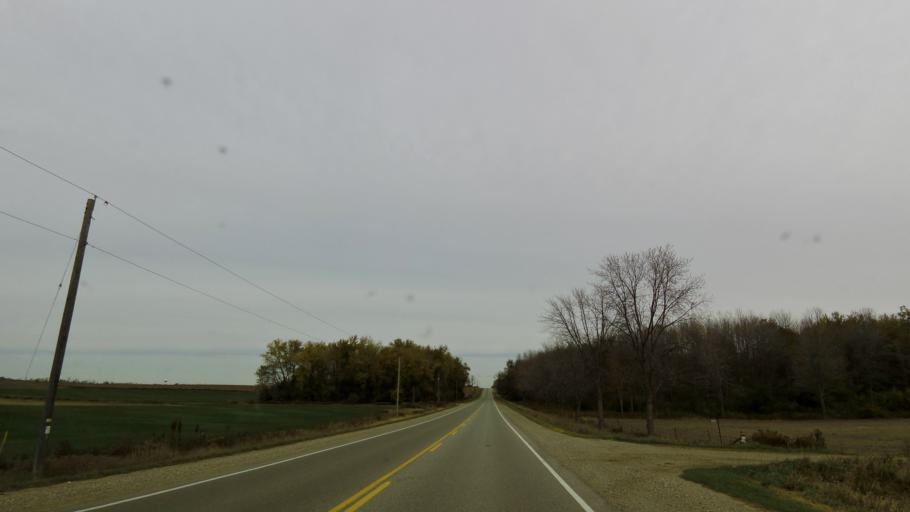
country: CA
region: Ontario
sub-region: Wellington County
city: Guelph
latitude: 43.5117
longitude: -80.3027
